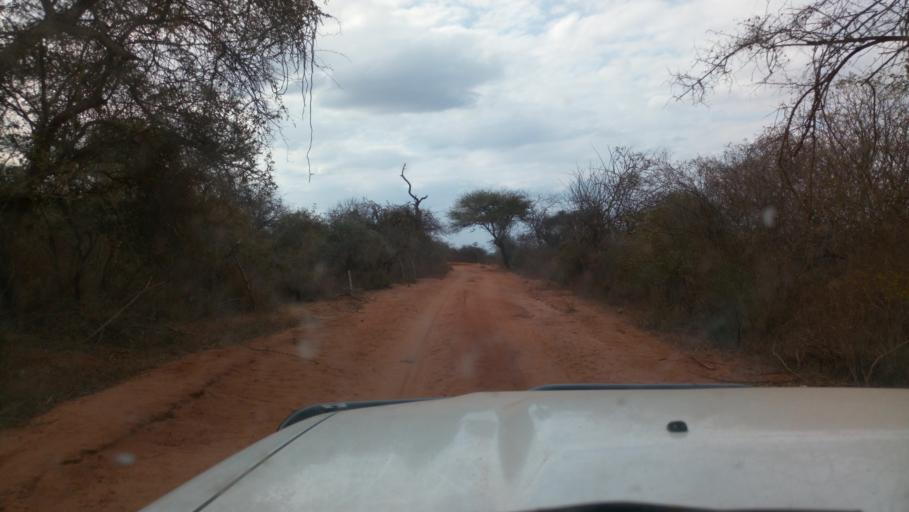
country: KE
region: Kitui
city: Kitui
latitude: -1.7602
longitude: 38.4398
